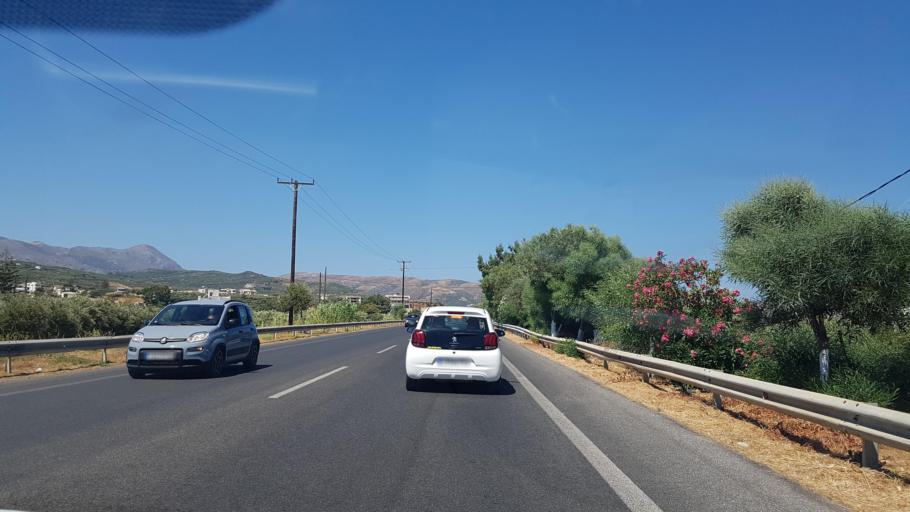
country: GR
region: Crete
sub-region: Nomos Chanias
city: Kissamos
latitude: 35.4969
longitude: 23.6928
